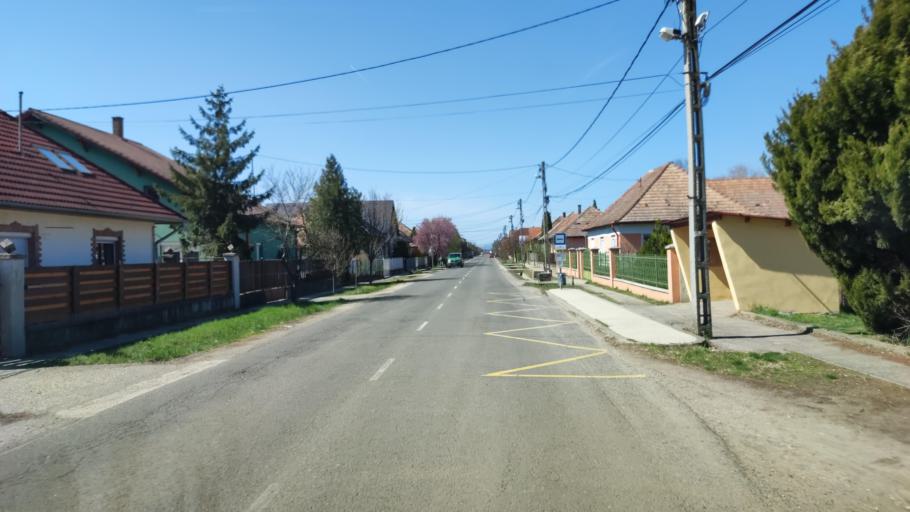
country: HU
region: Pest
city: Szod
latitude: 47.7195
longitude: 19.1810
